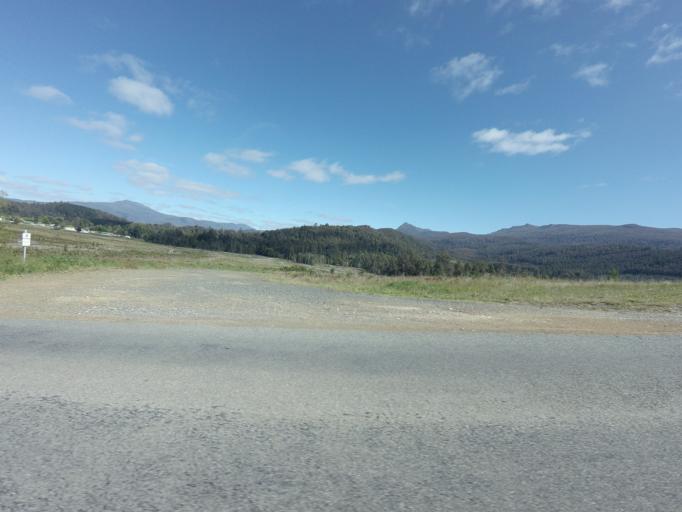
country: AU
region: Tasmania
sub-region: Derwent Valley
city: New Norfolk
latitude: -42.7519
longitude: 146.6362
